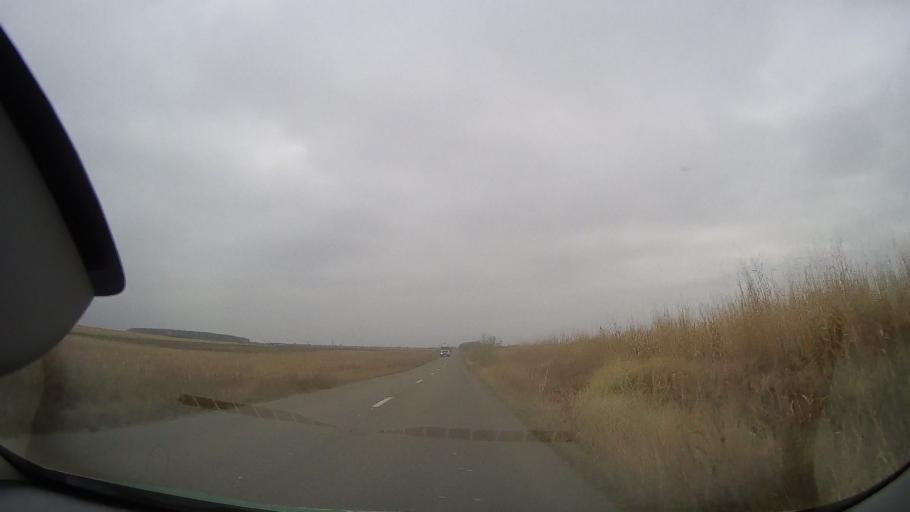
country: RO
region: Buzau
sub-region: Comuna Scutelnici
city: Scutelnici
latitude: 44.8696
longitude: 26.8896
